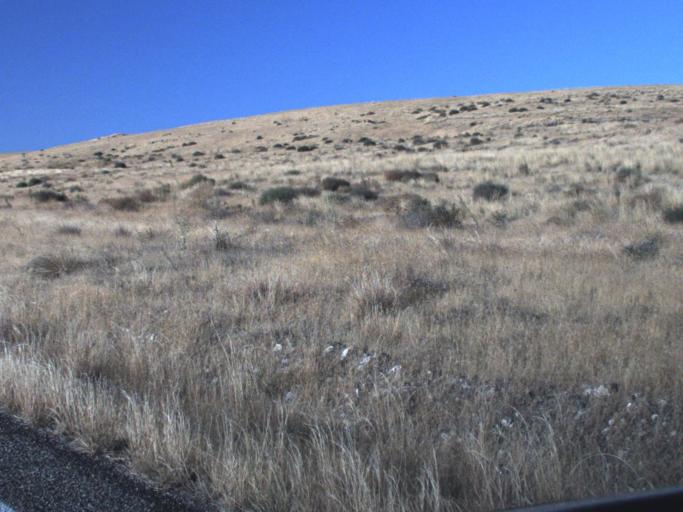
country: US
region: Washington
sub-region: Benton County
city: West Richland
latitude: 46.3743
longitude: -119.4448
